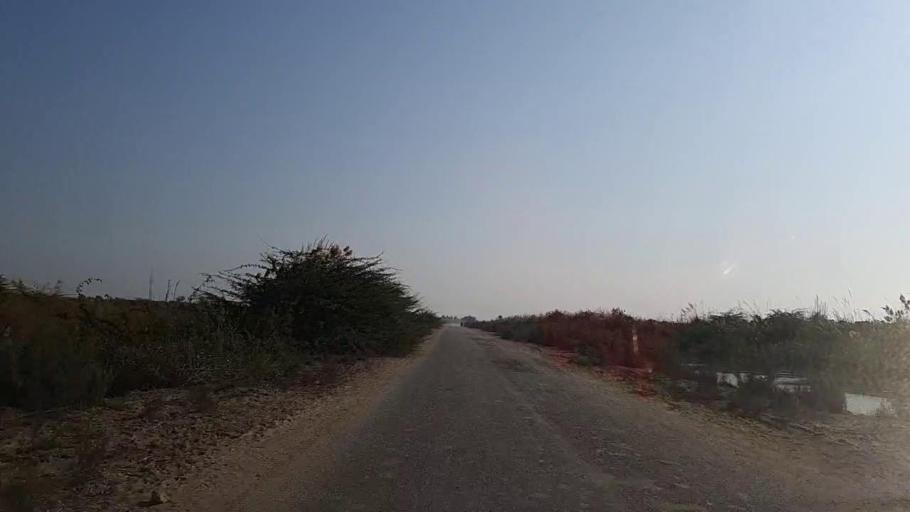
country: PK
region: Sindh
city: Tando Mittha Khan
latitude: 25.9103
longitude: 69.0760
